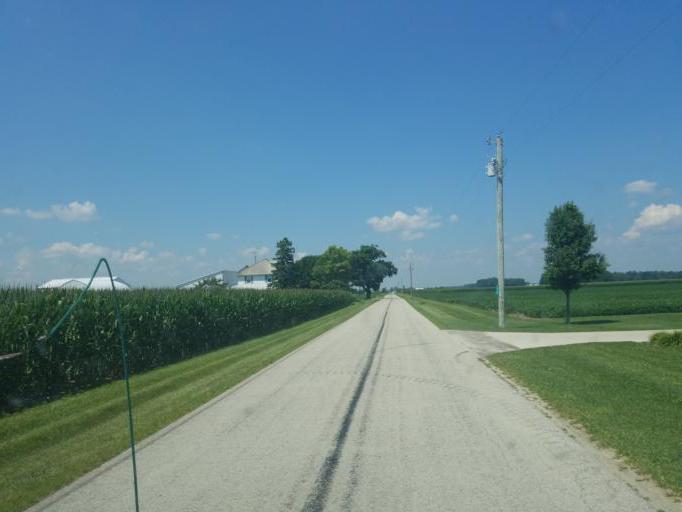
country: US
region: Ohio
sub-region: Shelby County
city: Jackson Center
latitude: 40.4024
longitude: -84.0691
